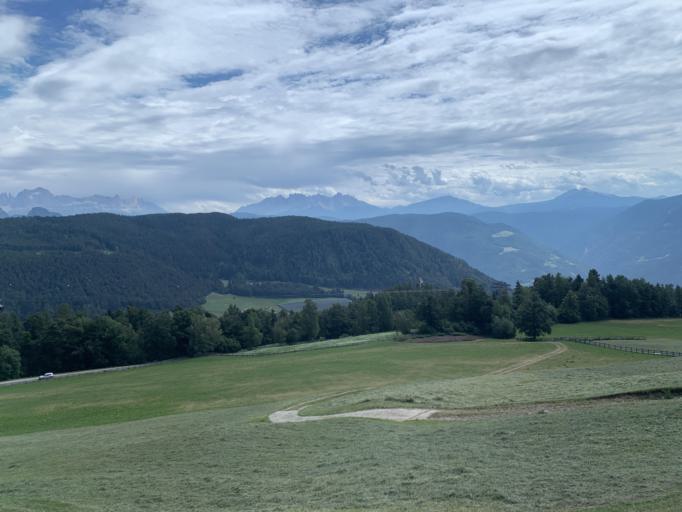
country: IT
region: Trentino-Alto Adige
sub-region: Bolzano
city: Soprabolzano
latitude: 46.5246
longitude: 11.3944
